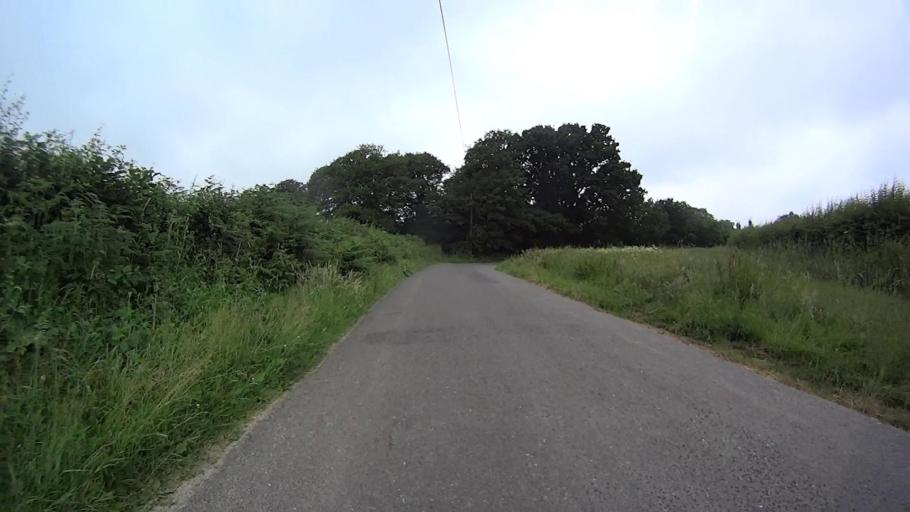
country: GB
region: England
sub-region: Surrey
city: Newdigate
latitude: 51.1115
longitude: -0.2896
